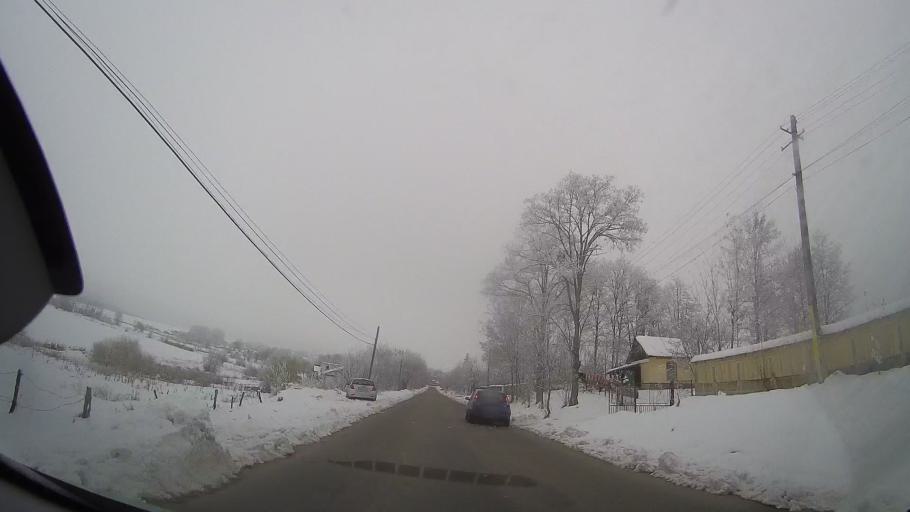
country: RO
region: Neamt
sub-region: Comuna Icusesti
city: Balusesti
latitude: 46.8586
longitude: 27.0227
